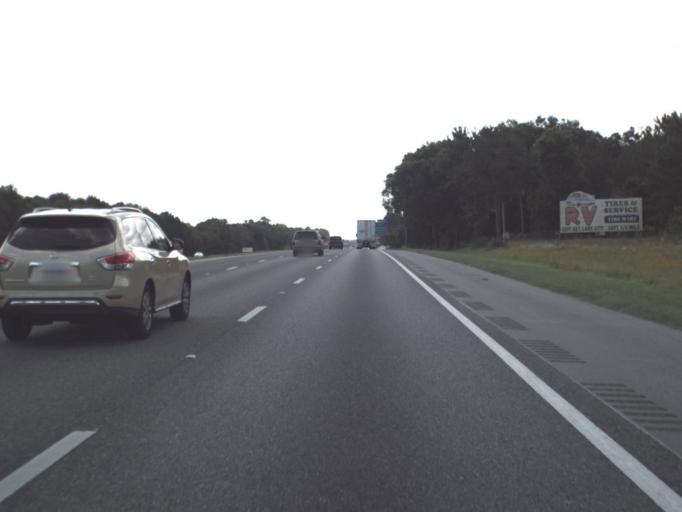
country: US
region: Florida
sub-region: Suwannee County
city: Wellborn
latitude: 30.2960
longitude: -82.7833
